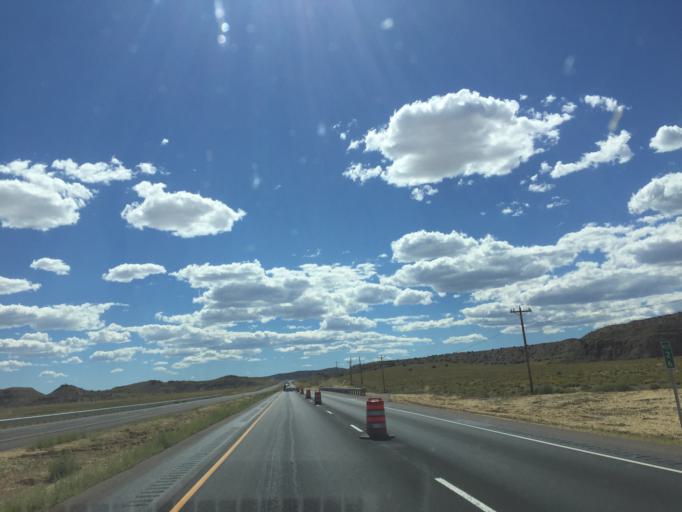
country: US
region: New Mexico
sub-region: McKinley County
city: Twin Lakes
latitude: 35.8718
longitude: -108.7110
